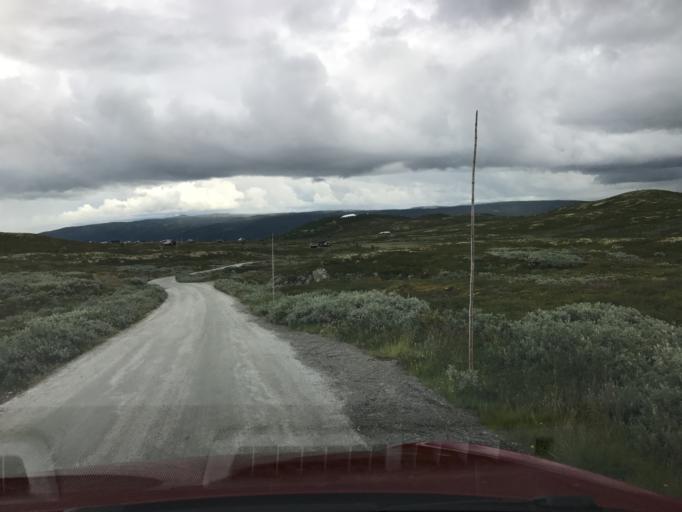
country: NO
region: Buskerud
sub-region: Hol
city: Geilo
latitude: 60.5464
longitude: 8.1583
